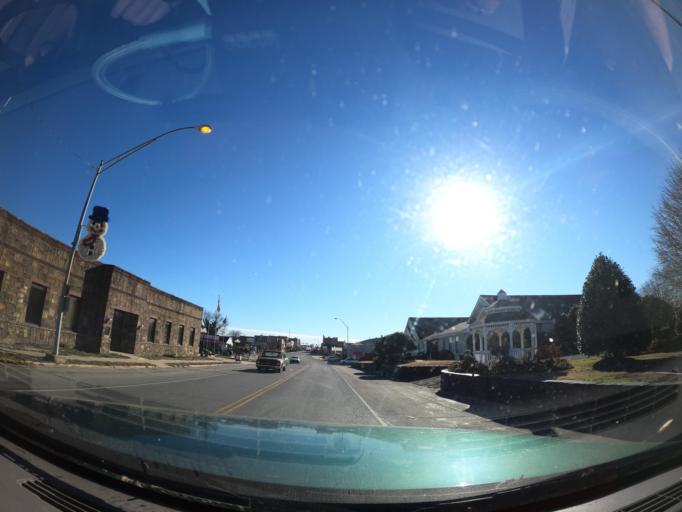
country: US
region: Oklahoma
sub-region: McIntosh County
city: Eufaula
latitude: 35.2896
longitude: -95.5825
